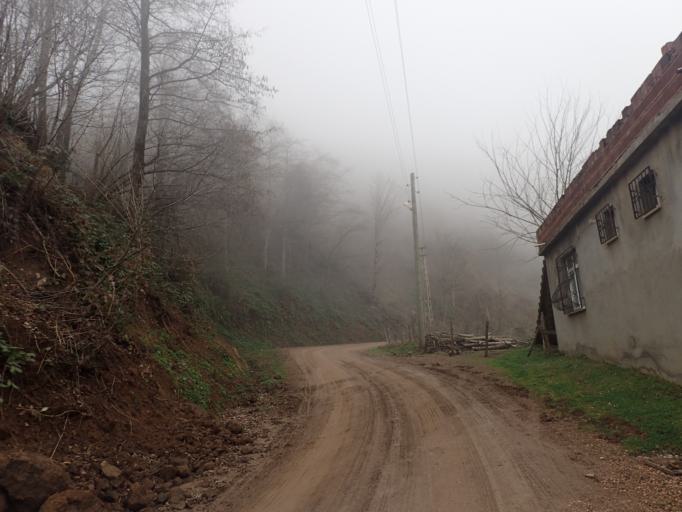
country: TR
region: Ordu
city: Camas
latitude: 40.9047
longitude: 37.5665
